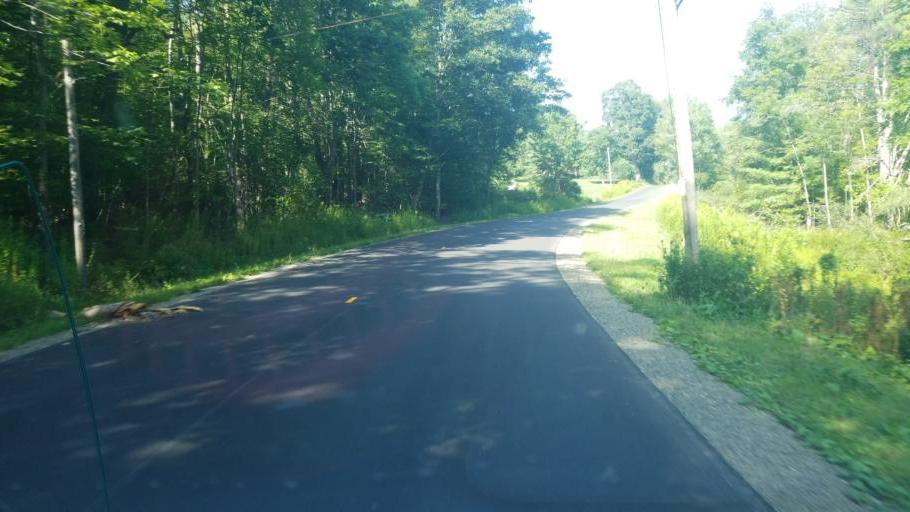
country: US
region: New York
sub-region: Allegany County
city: Wellsville
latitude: 42.0628
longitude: -78.0395
